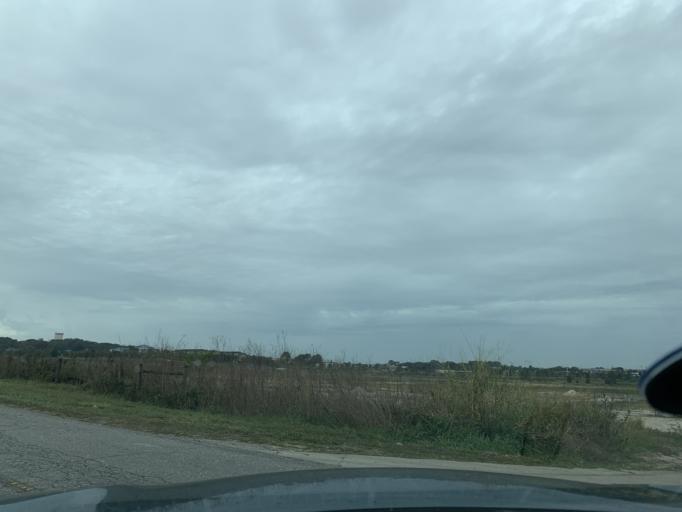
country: US
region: Florida
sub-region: Pasco County
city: Zephyrhills North
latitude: 28.2713
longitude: -82.1798
